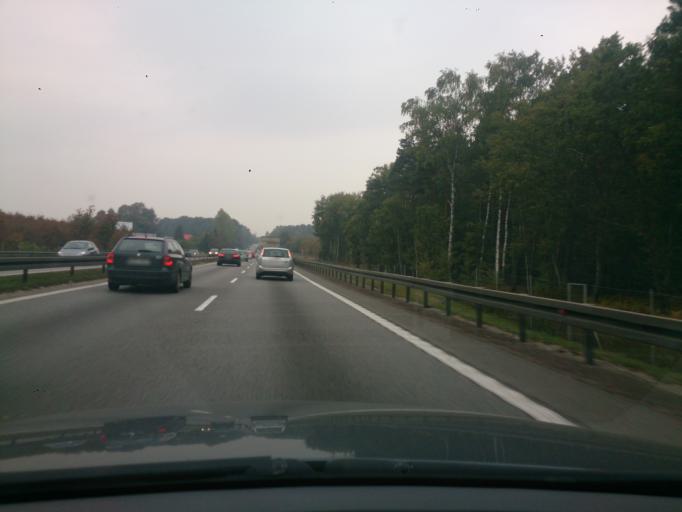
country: PL
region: Pomeranian Voivodeship
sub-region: Sopot
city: Sopot
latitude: 54.3851
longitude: 18.5025
